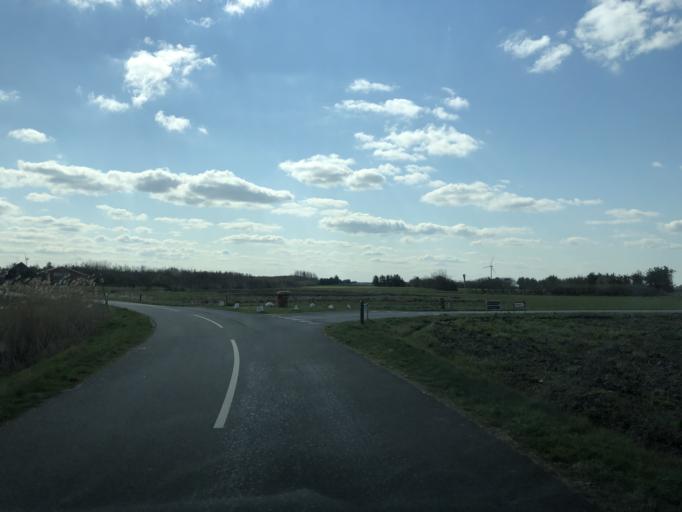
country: DK
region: Central Jutland
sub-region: Holstebro Kommune
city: Ulfborg
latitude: 56.3970
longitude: 8.2223
